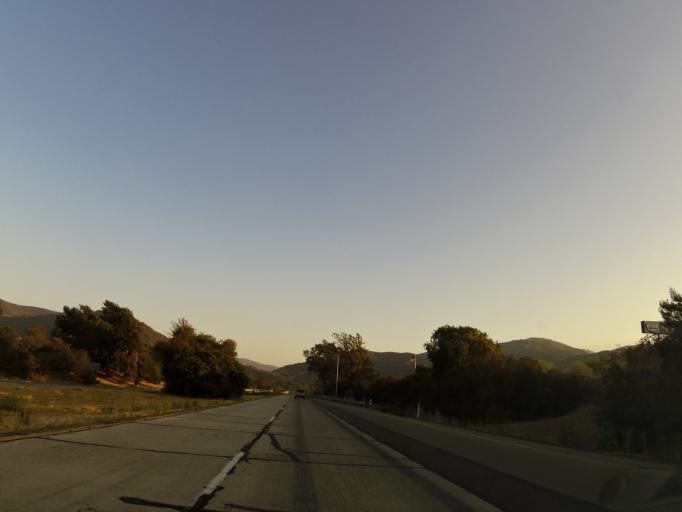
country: US
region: California
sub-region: Santa Barbara County
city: Buellton
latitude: 34.6102
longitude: -120.1909
